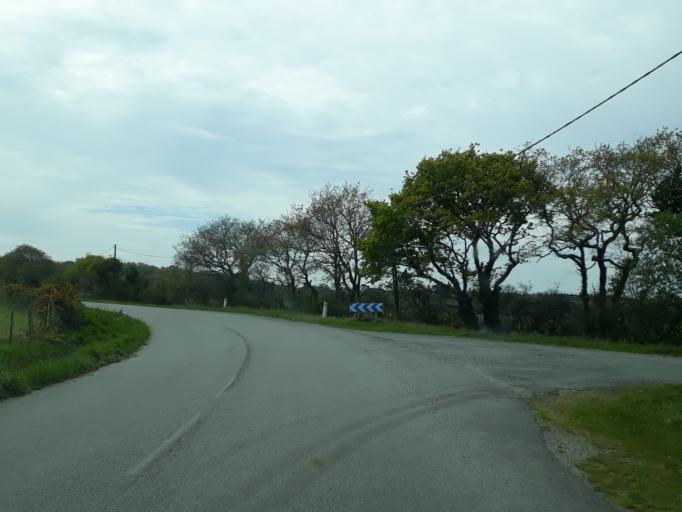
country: FR
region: Pays de la Loire
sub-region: Departement de la Loire-Atlantique
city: Saint-Molf
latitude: 47.3693
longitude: -2.4112
